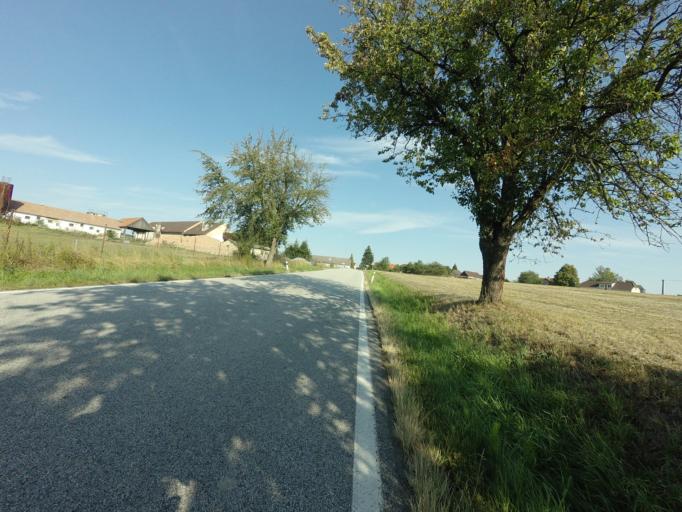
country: CZ
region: Jihocesky
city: Tyn nad Vltavou
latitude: 49.2765
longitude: 14.4009
